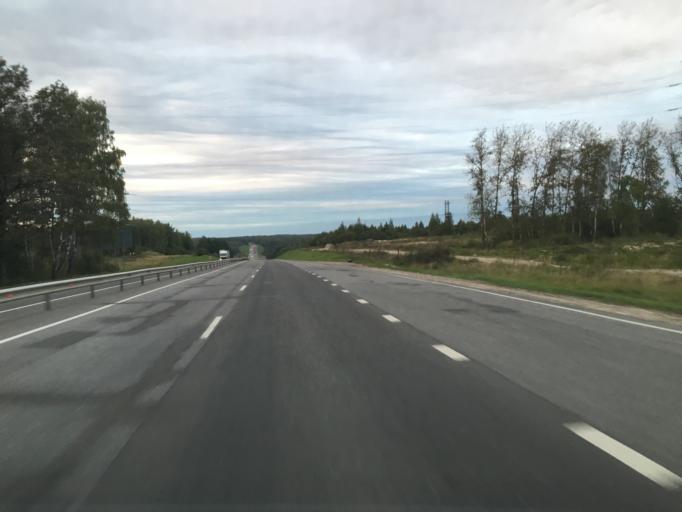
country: RU
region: Kaluga
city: Kaluga
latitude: 54.5904
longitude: 36.3300
